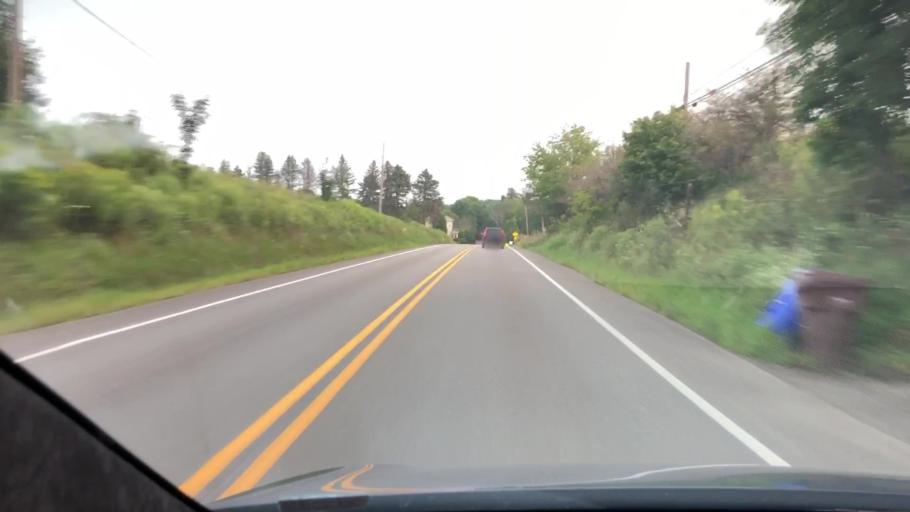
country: US
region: Pennsylvania
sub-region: Butler County
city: Slippery Rock
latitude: 41.1129
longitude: -80.0068
